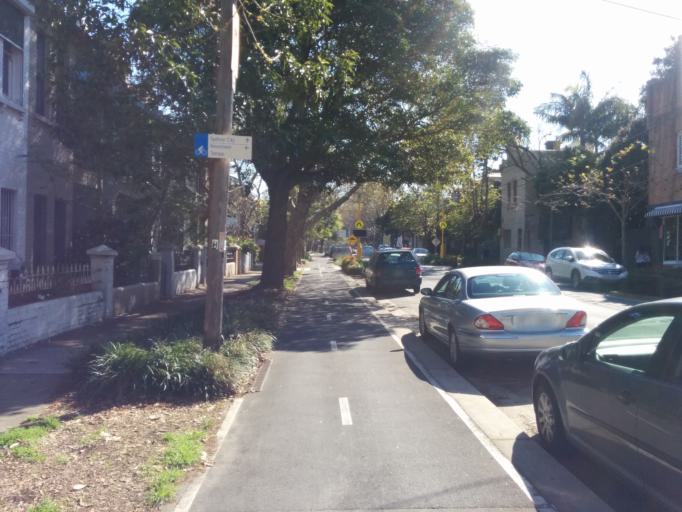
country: AU
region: New South Wales
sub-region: City of Sydney
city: Redfern
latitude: -33.8951
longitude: 151.2136
